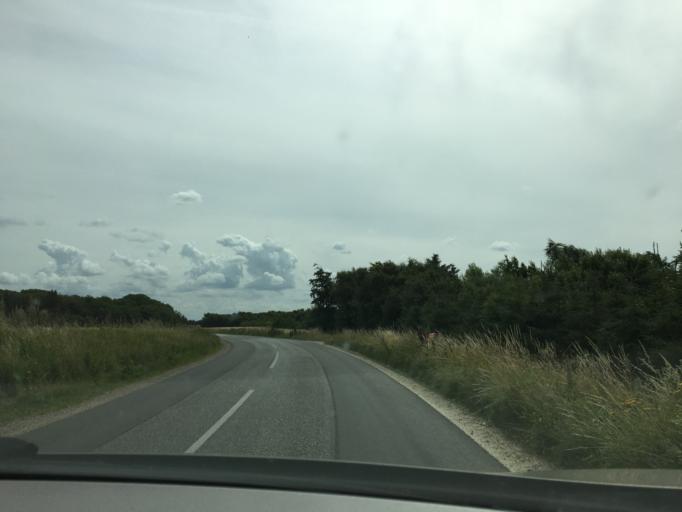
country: DK
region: Central Jutland
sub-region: Ringkobing-Skjern Kommune
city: Ringkobing
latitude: 55.9855
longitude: 8.3400
